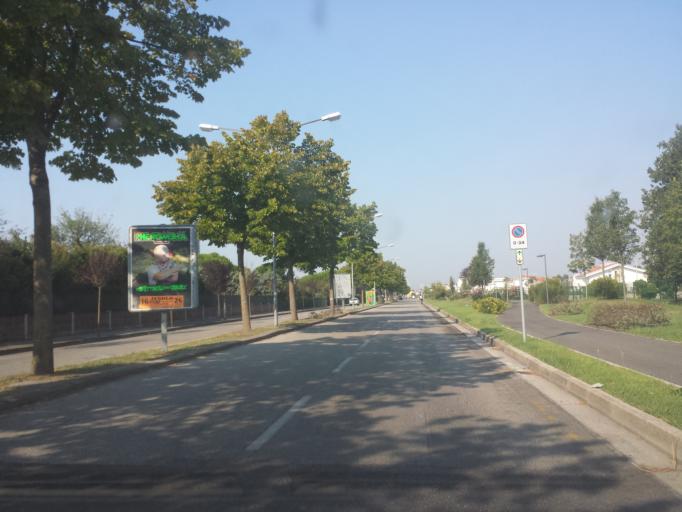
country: IT
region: Veneto
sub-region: Provincia di Venezia
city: Lido di Iesolo
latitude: 45.5020
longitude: 12.6263
